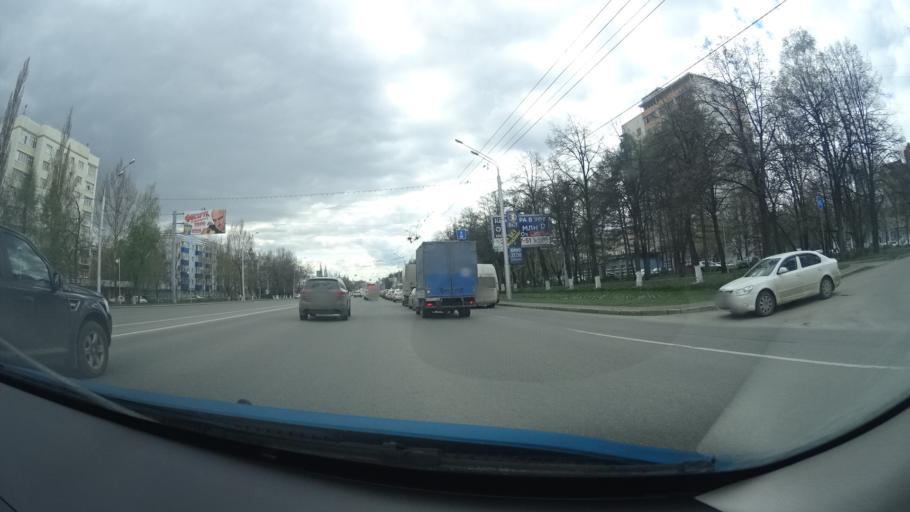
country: RU
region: Bashkortostan
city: Ufa
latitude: 54.7577
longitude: 56.0073
